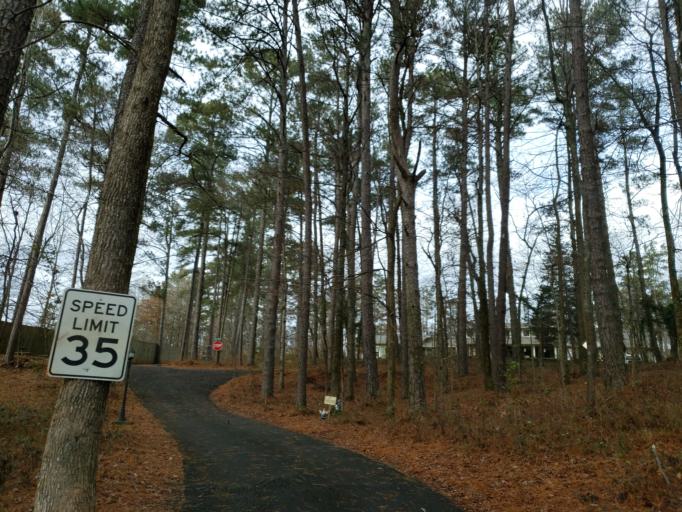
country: US
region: Georgia
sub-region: Cobb County
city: Fair Oaks
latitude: 33.9158
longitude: -84.6113
